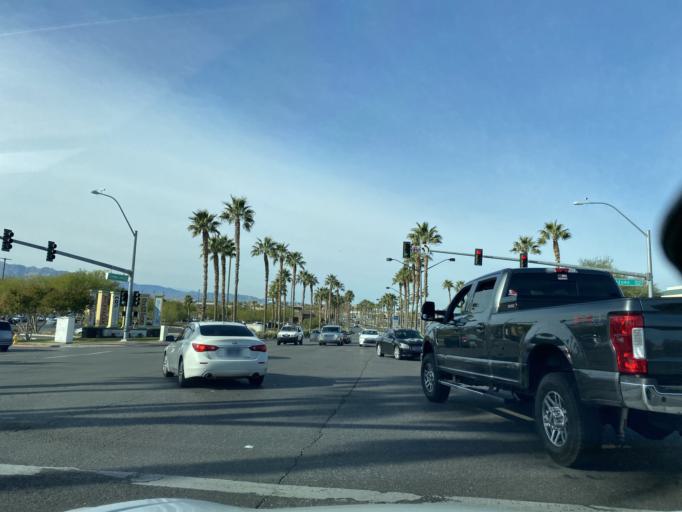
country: US
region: Nevada
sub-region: Clark County
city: Las Vegas
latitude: 36.2715
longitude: -115.2643
